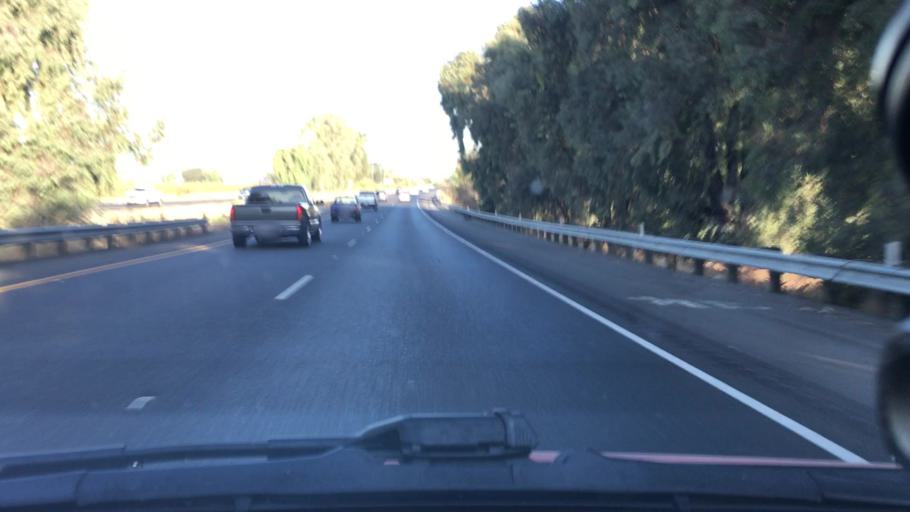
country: US
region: California
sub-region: Sacramento County
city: Elk Grove
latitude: 38.3654
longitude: -121.3505
